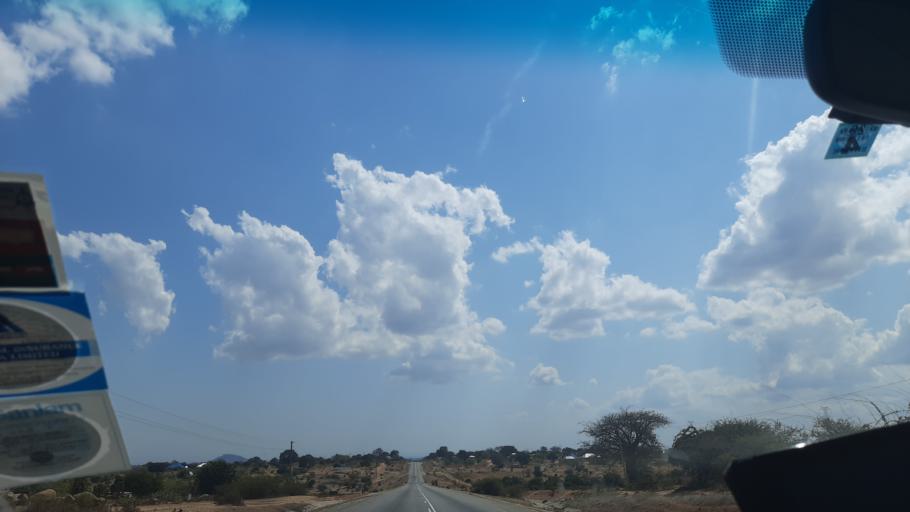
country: TZ
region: Singida
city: Kintinku
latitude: -6.0156
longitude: 35.4428
